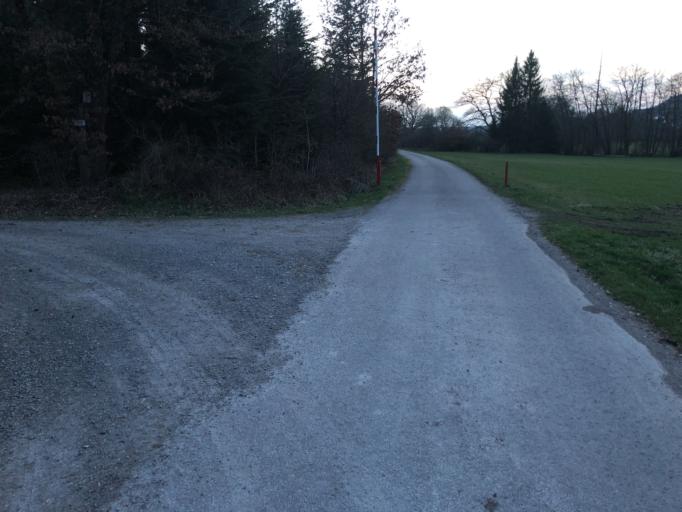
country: DE
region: Baden-Wuerttemberg
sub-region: Tuebingen Region
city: Bodelshausen
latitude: 48.4294
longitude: 8.9533
